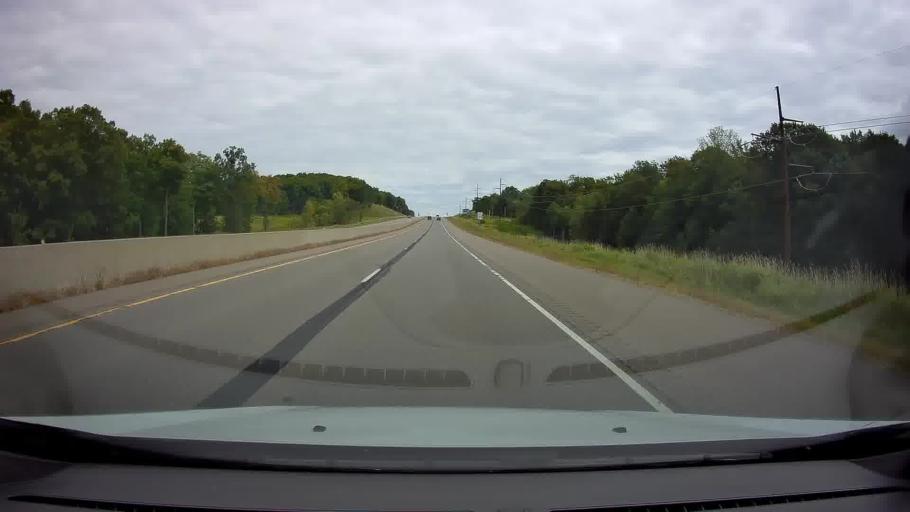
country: US
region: Wisconsin
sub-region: Marathon County
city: Marathon
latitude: 44.9442
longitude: -89.7749
